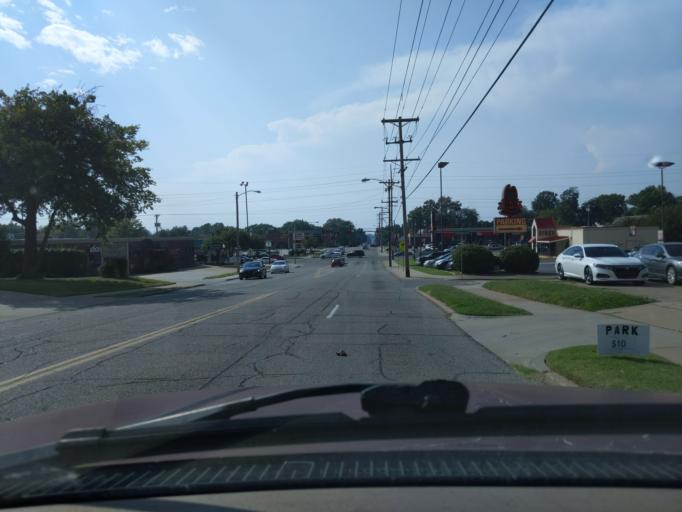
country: US
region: Oklahoma
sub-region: Tulsa County
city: Tulsa
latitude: 36.1333
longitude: -95.9388
